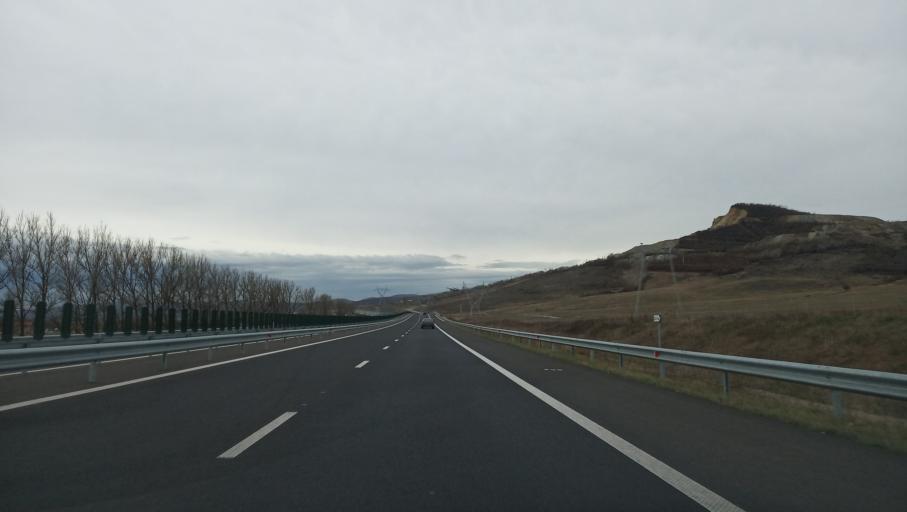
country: RO
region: Hunedoara
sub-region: Comuna Branisca
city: Branisca
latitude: 45.9421
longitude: 22.7313
